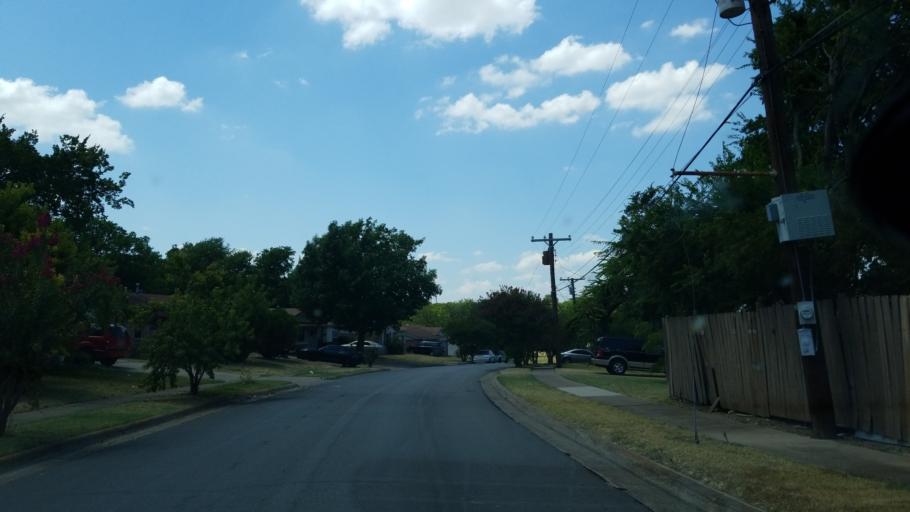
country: US
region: Texas
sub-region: Dallas County
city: Duncanville
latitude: 32.6680
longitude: -96.8955
